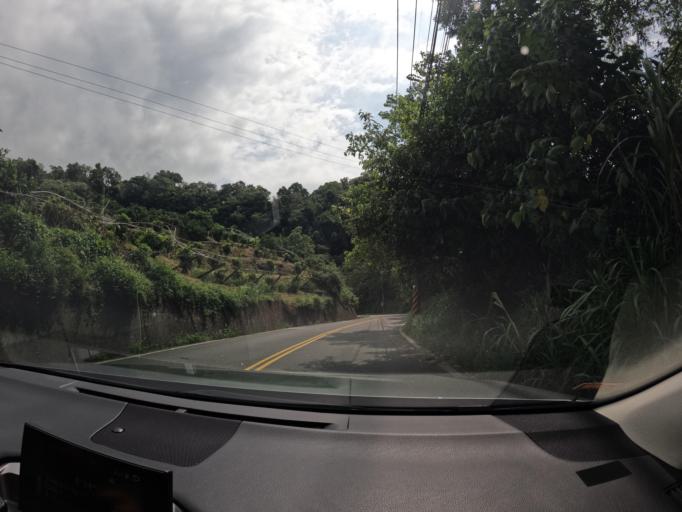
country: TW
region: Taiwan
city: Fengyuan
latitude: 24.3143
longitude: 120.8632
